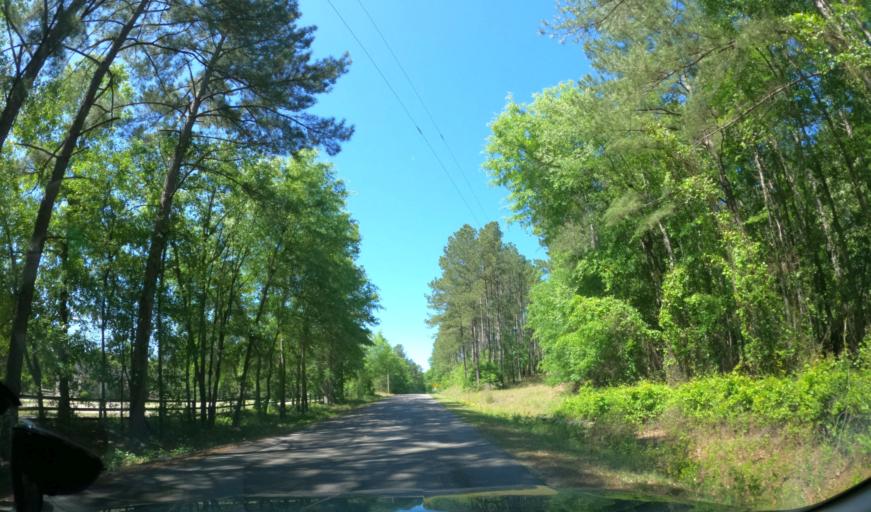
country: US
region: South Carolina
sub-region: Aiken County
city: Langley
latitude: 33.4513
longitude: -81.7973
